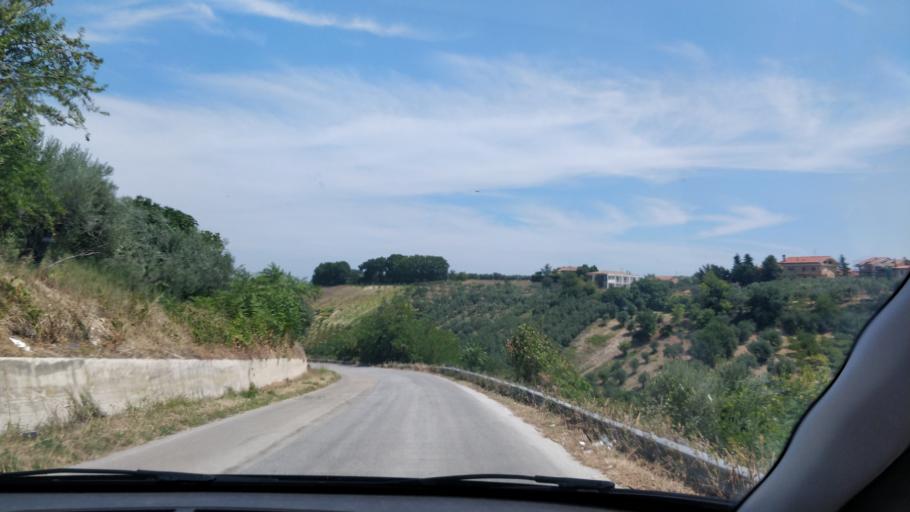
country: IT
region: Abruzzo
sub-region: Provincia di Chieti
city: Torrevecchia
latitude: 42.3981
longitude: 14.2031
